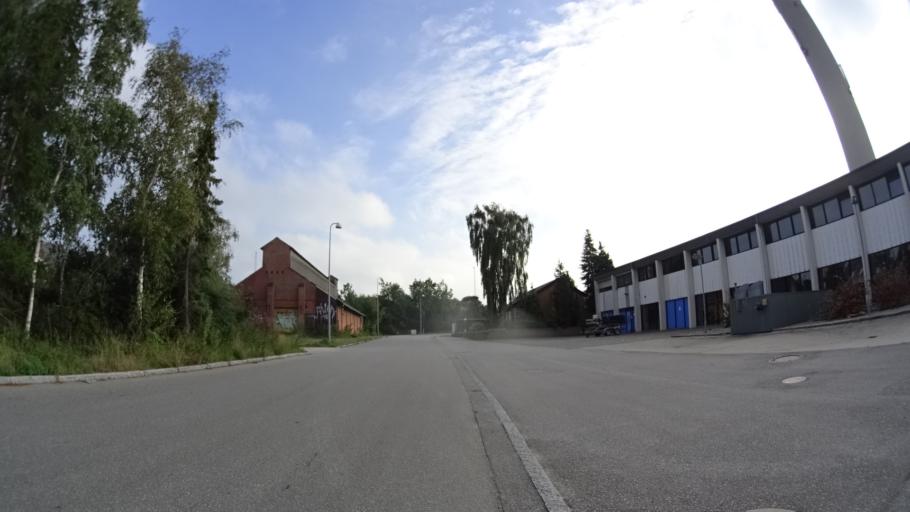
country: DK
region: Central Jutland
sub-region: Arhus Kommune
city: Arhus
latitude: 56.1364
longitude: 10.1728
